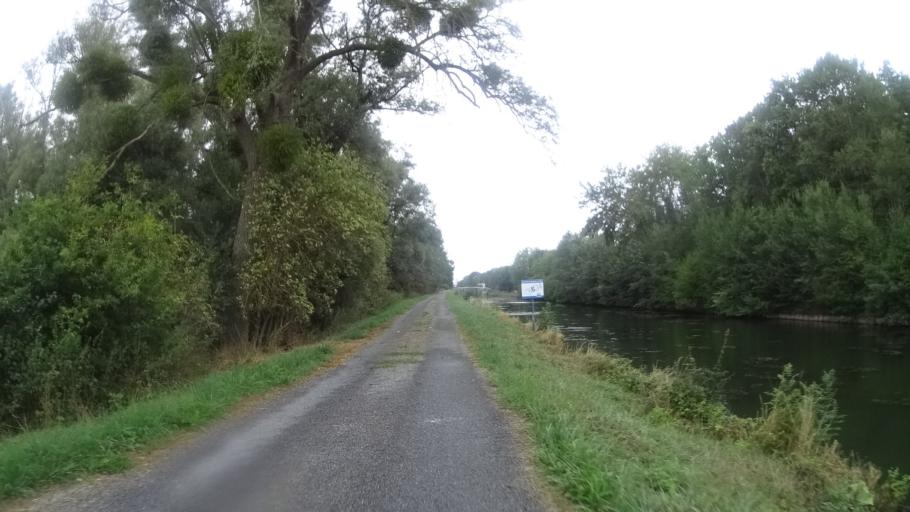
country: FR
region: Picardie
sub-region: Departement de l'Aisne
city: Ribemont
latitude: 49.8222
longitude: 3.4671
